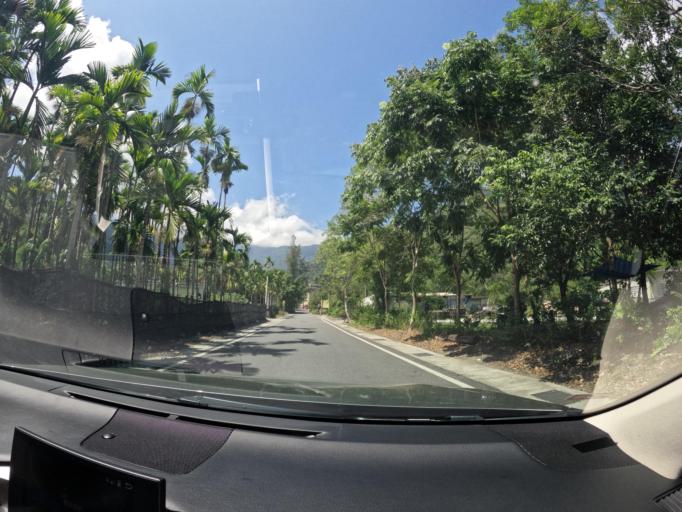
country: TW
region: Taiwan
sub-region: Hualien
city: Hualian
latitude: 23.7186
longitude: 121.4070
